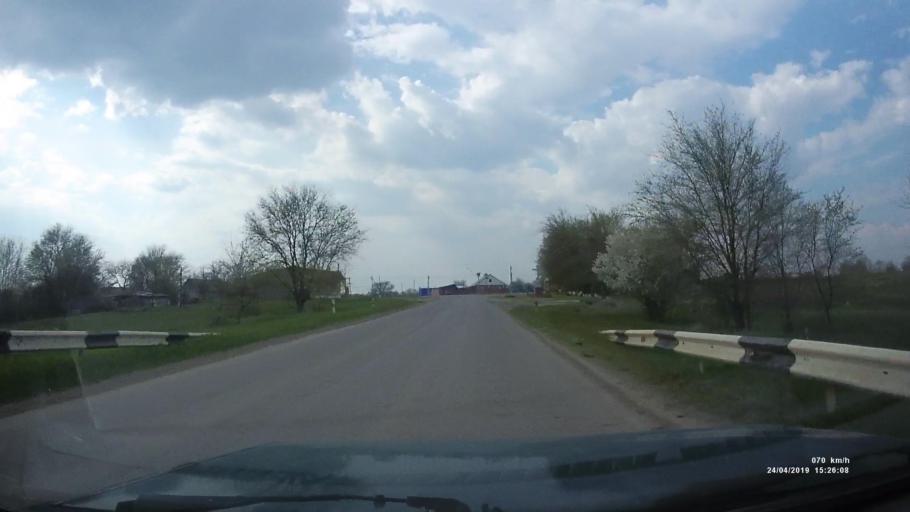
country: RU
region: Rostov
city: Remontnoye
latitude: 46.5567
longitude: 43.0367
